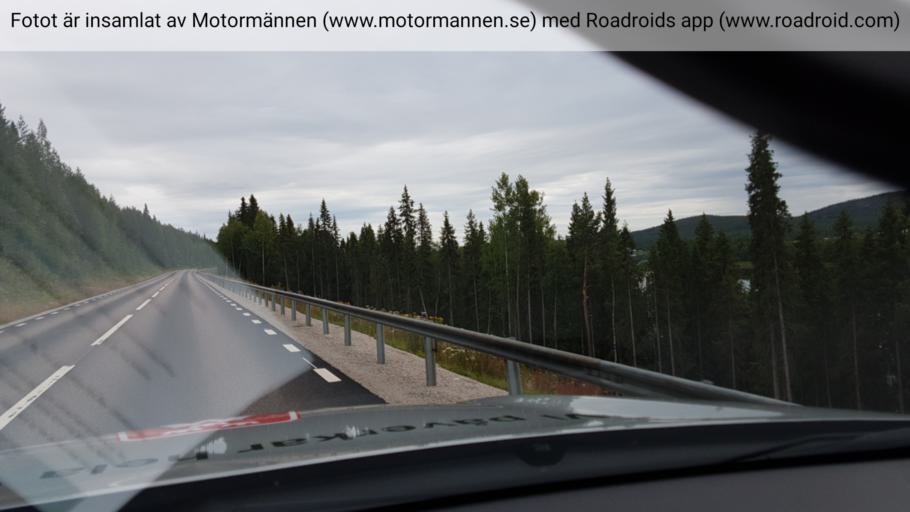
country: SE
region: Norrbotten
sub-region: Overkalix Kommun
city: OEverkalix
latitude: 66.4779
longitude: 22.7876
